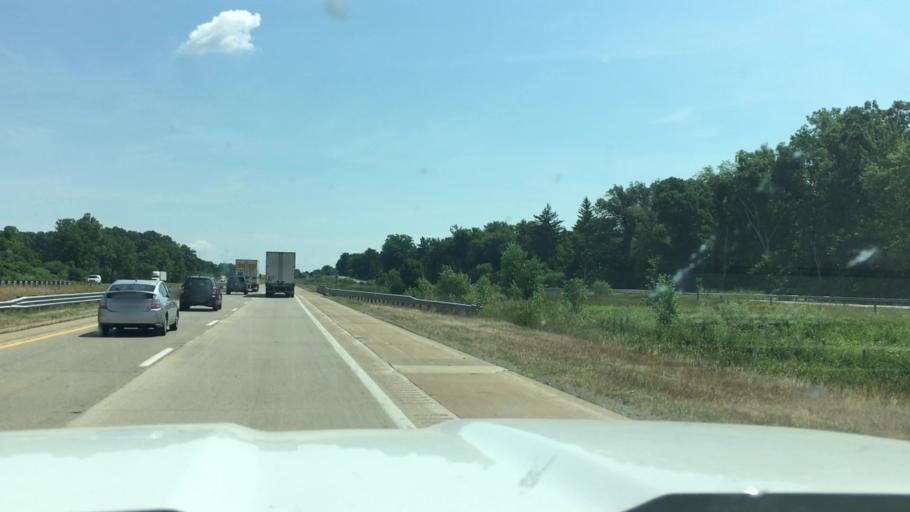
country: US
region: Michigan
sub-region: Ingham County
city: Haslett
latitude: 42.8019
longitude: -84.3398
